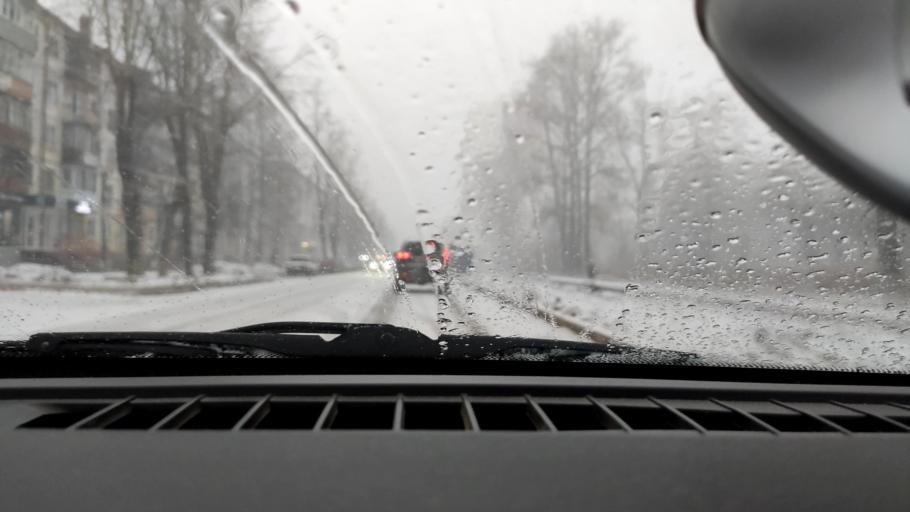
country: RU
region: Perm
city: Perm
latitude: 57.9735
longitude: 56.2755
